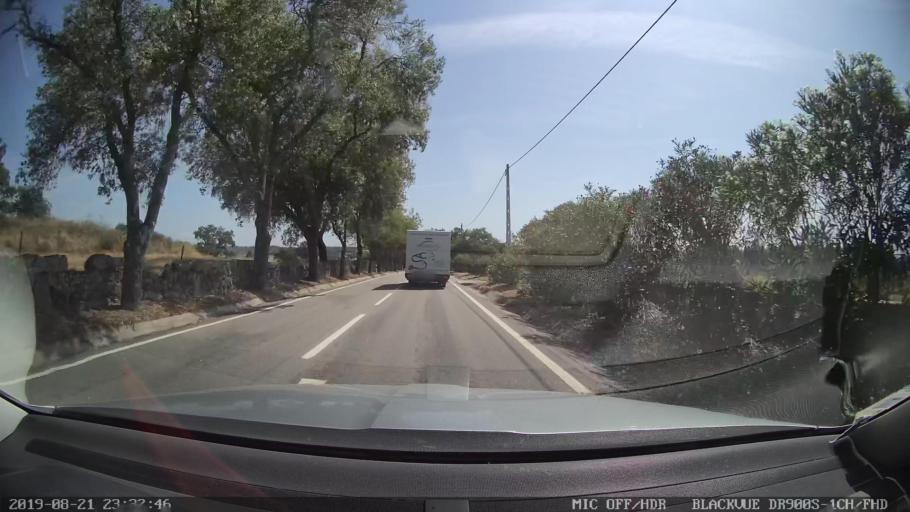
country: PT
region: Guarda
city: Alcains
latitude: 39.8808
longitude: -7.4084
